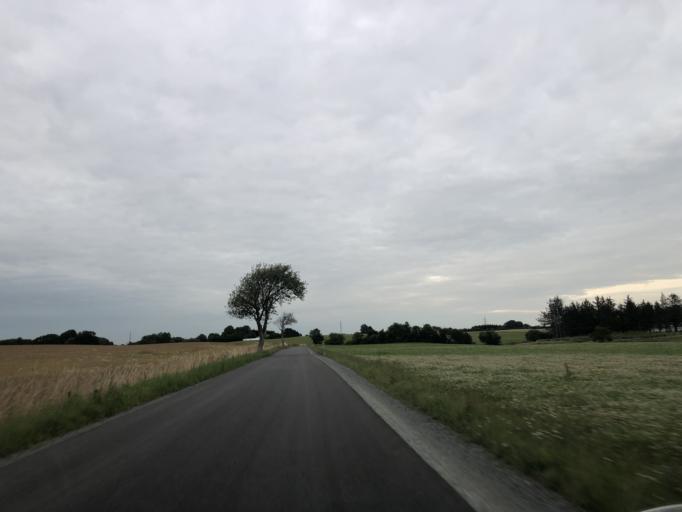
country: DK
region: South Denmark
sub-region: Vejle Kommune
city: Jelling
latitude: 55.7164
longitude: 9.3914
